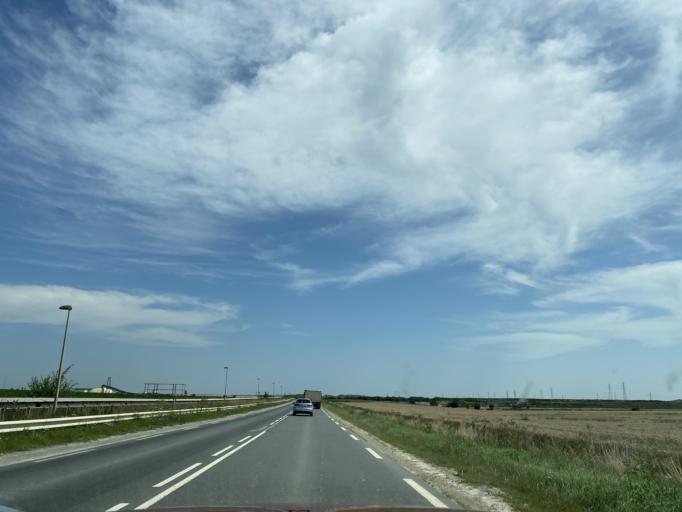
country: FR
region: Centre
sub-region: Departement d'Eure-et-Loir
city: Voves
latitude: 48.2903
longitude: 1.7146
